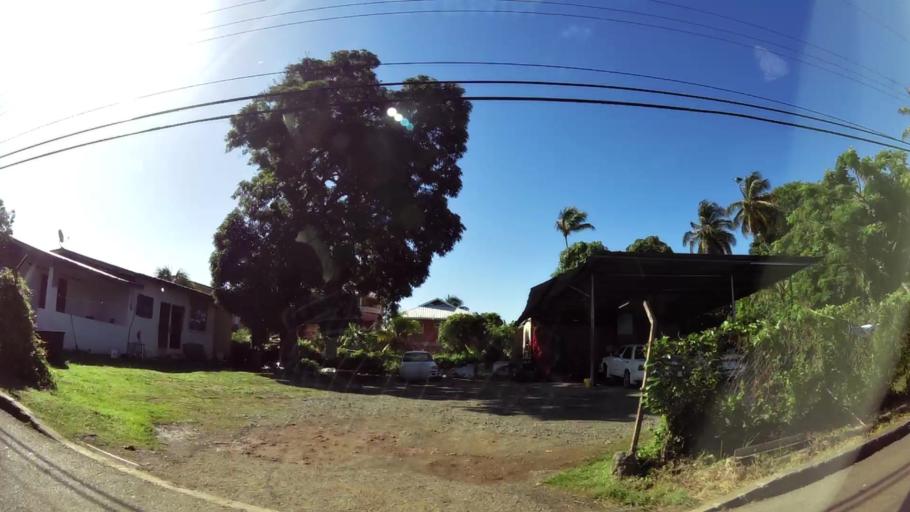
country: TT
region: Tobago
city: Scarborough
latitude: 11.1619
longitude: -60.8076
